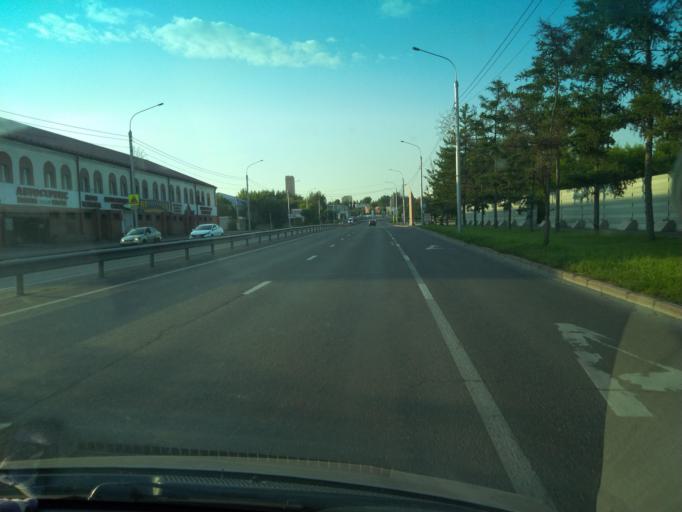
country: RU
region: Krasnoyarskiy
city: Krasnoyarsk
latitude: 56.0211
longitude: 92.8853
